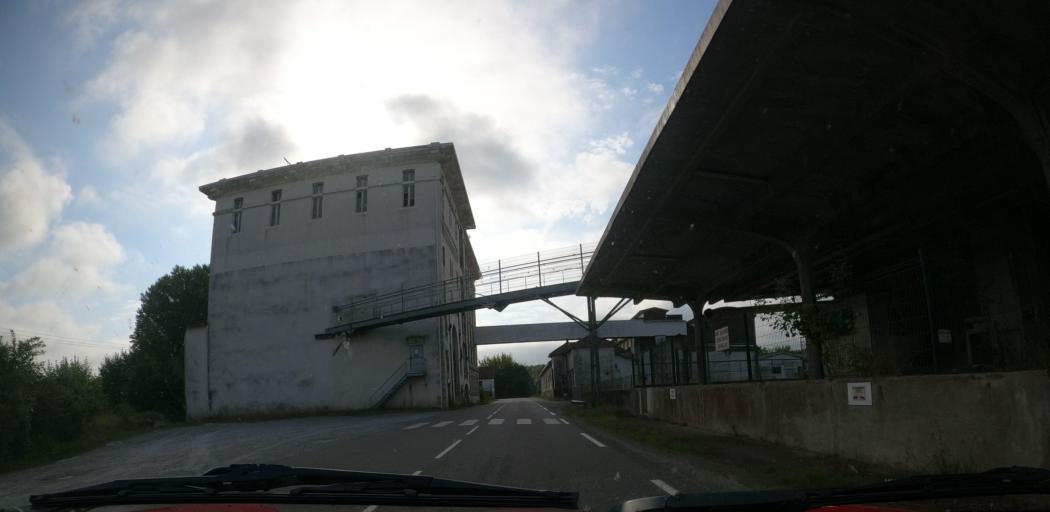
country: FR
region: Aquitaine
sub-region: Departement des Landes
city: Peyrehorade
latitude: 43.5423
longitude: -1.0958
